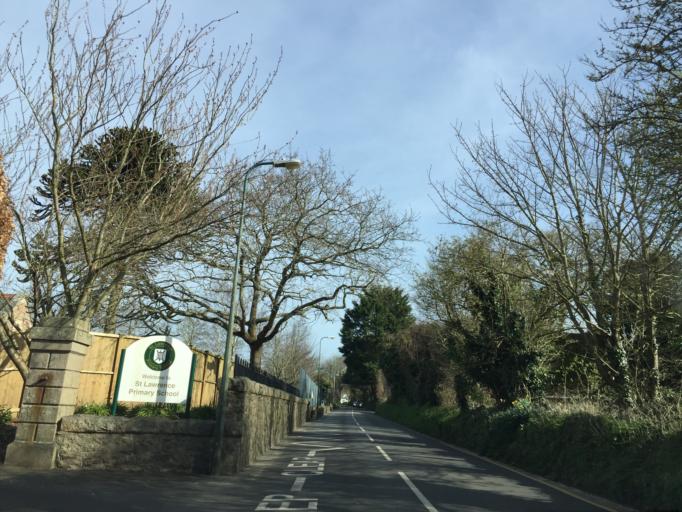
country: JE
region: St Helier
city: Saint Helier
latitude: 49.2159
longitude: -2.1409
